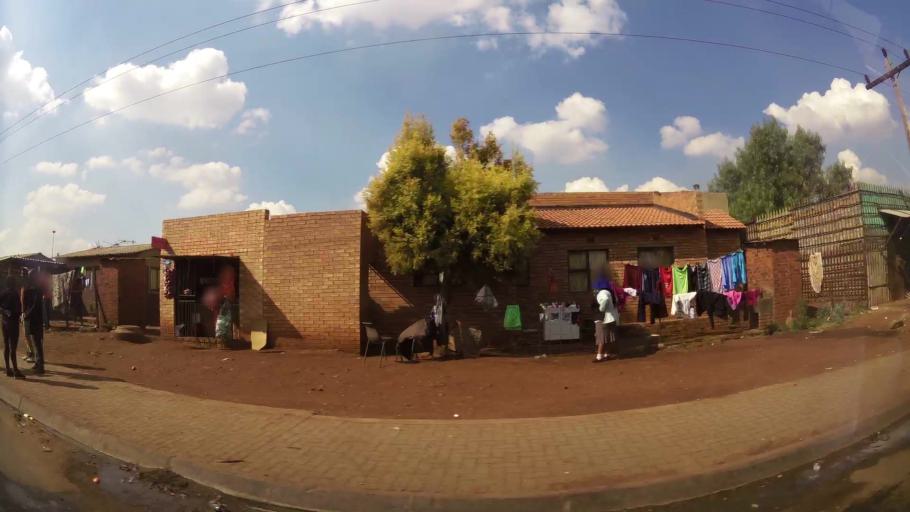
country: ZA
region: Gauteng
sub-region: Ekurhuleni Metropolitan Municipality
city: Germiston
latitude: -26.3188
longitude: 28.1439
